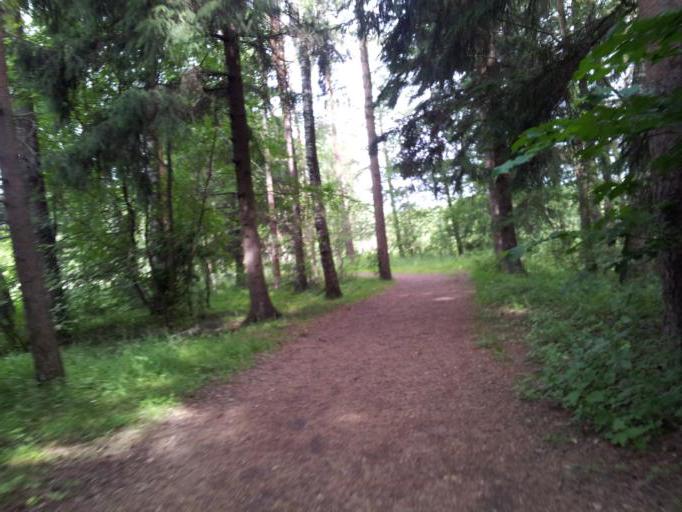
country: SE
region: Uppsala
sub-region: Uppsala Kommun
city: Gamla Uppsala
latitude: 59.8888
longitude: 17.6613
